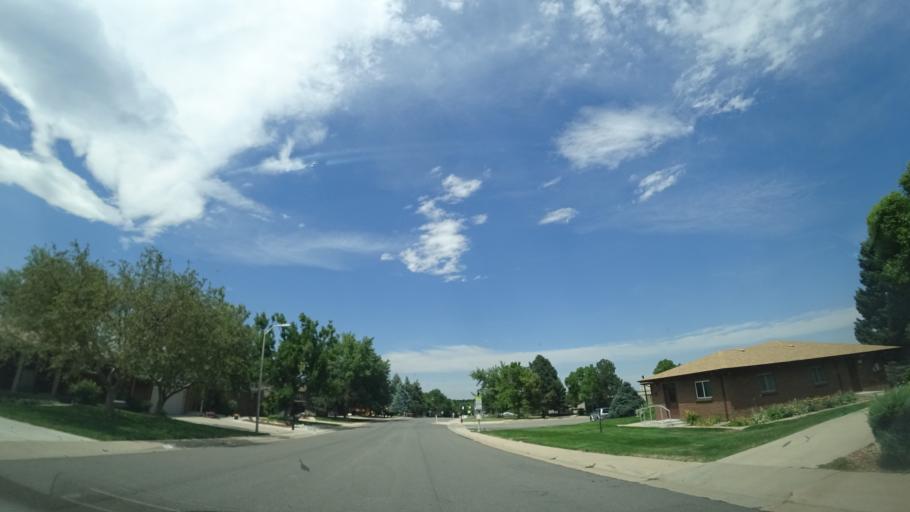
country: US
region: Colorado
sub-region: Jefferson County
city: Lakewood
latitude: 39.6908
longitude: -105.1053
